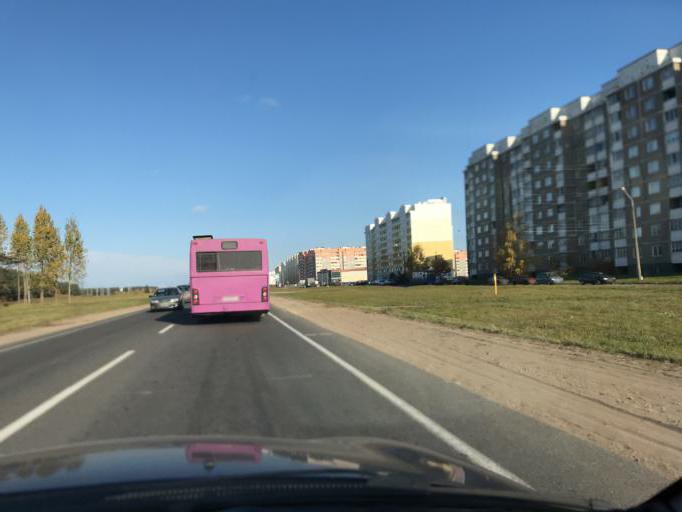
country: BY
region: Grodnenskaya
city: Lida
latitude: 53.8950
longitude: 25.2516
